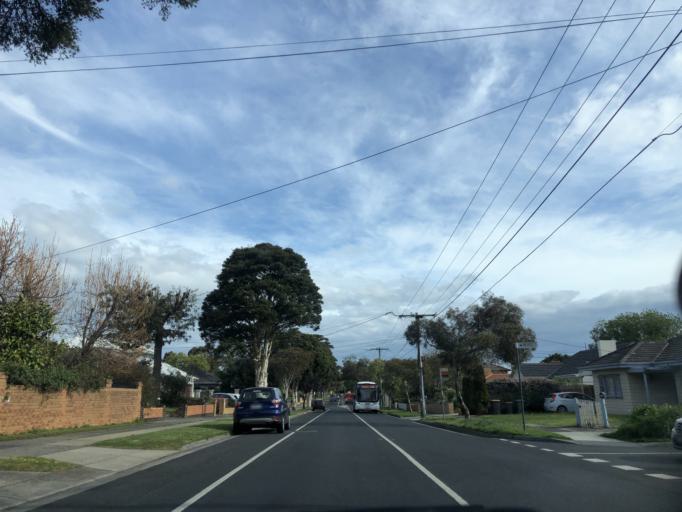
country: AU
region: Victoria
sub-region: Monash
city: Oakleigh South
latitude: -37.9175
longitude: 145.0882
